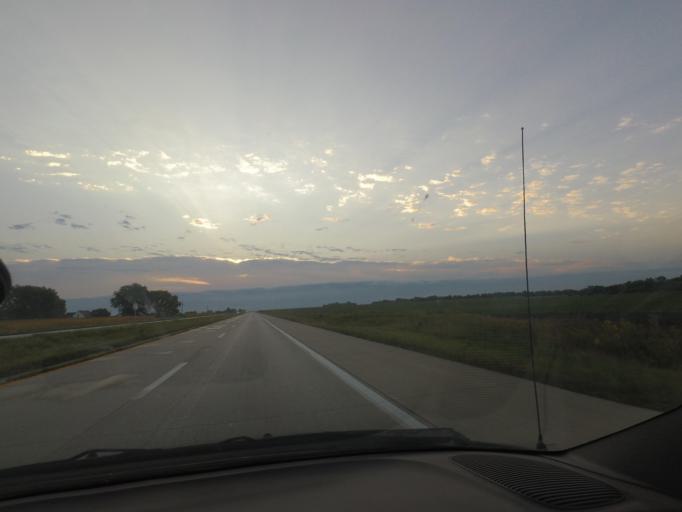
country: US
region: Missouri
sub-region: Macon County
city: Macon
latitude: 39.7502
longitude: -92.3511
